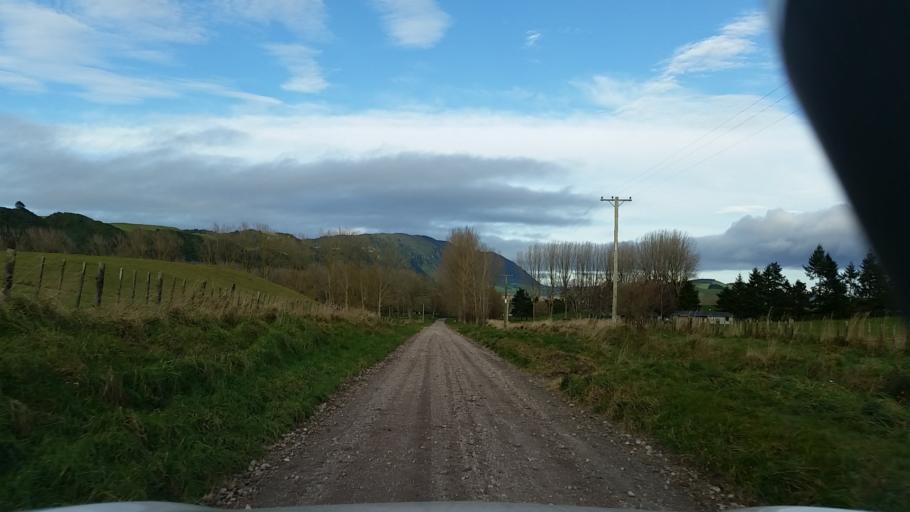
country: NZ
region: Bay of Plenty
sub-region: Rotorua District
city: Rotorua
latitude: -38.3196
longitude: 176.2985
